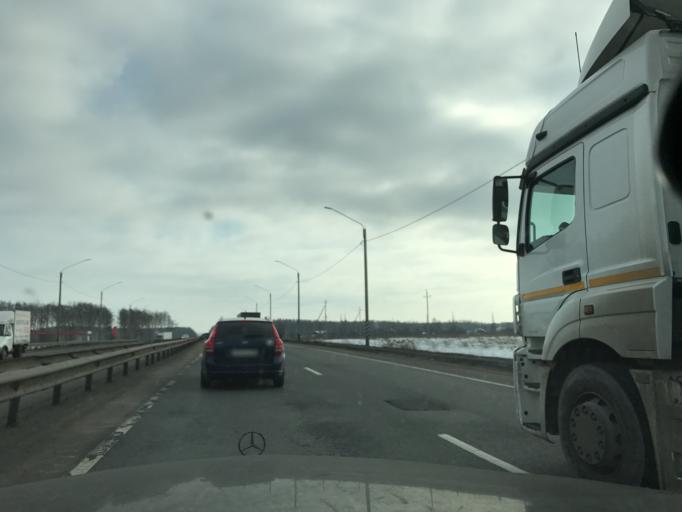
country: RU
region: Vladimir
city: Vyazniki
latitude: 56.2215
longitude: 42.1409
